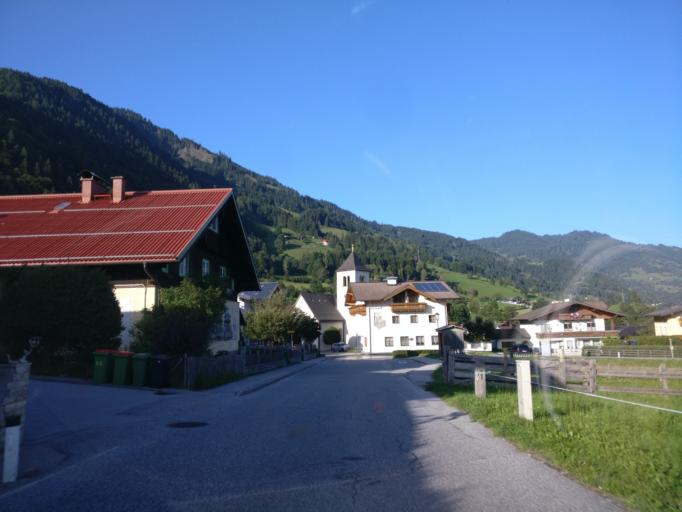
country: AT
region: Salzburg
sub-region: Politischer Bezirk Sankt Johann im Pongau
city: Goldegg
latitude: 47.3290
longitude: 13.0788
